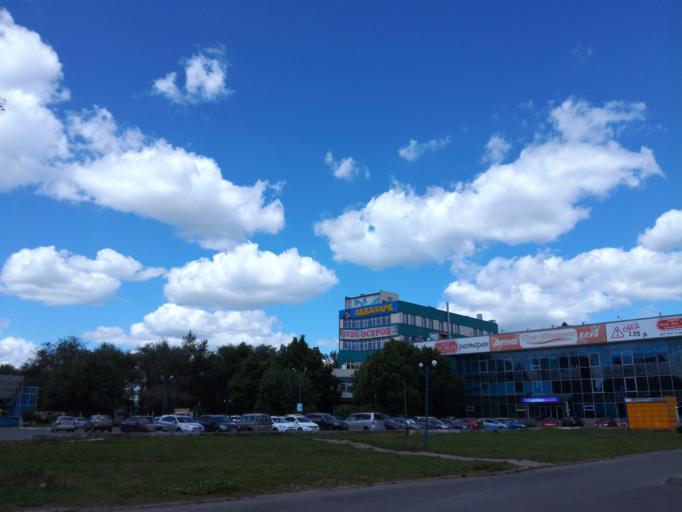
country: RU
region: Kursk
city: Kursk
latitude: 51.7465
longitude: 36.2537
